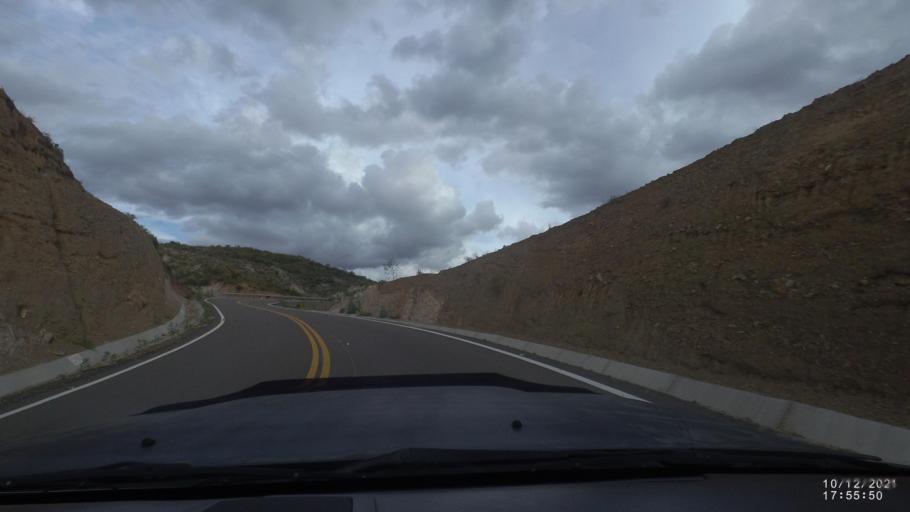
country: BO
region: Cochabamba
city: Cliza
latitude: -17.7138
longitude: -65.9417
